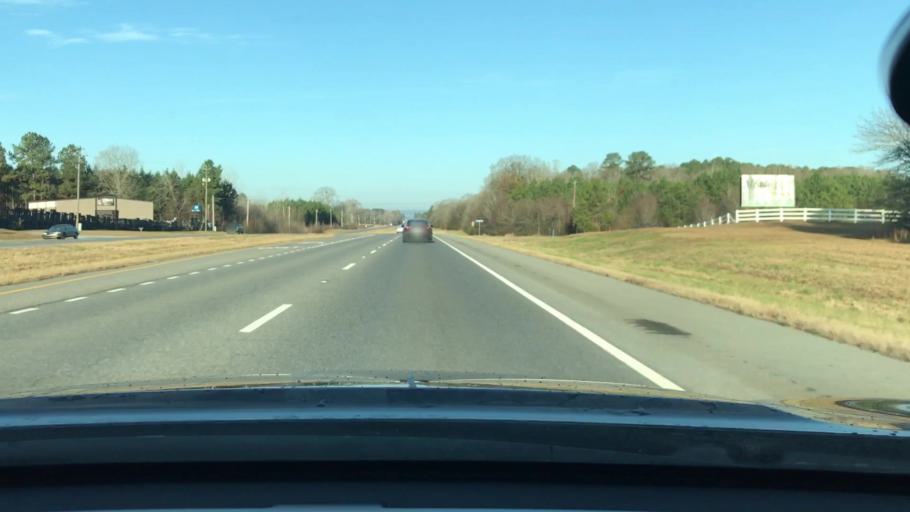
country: US
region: Alabama
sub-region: Shelby County
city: Harpersville
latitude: 33.3200
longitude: -86.3988
